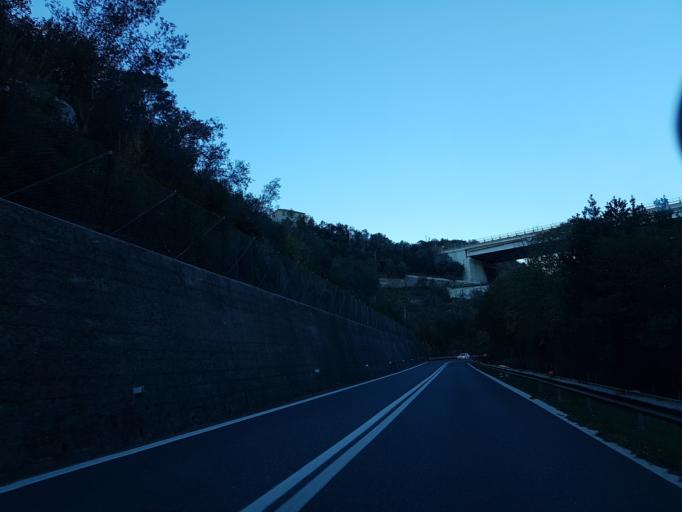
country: IT
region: Liguria
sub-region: Provincia di Genova
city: Recco
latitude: 44.3729
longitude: 9.1490
